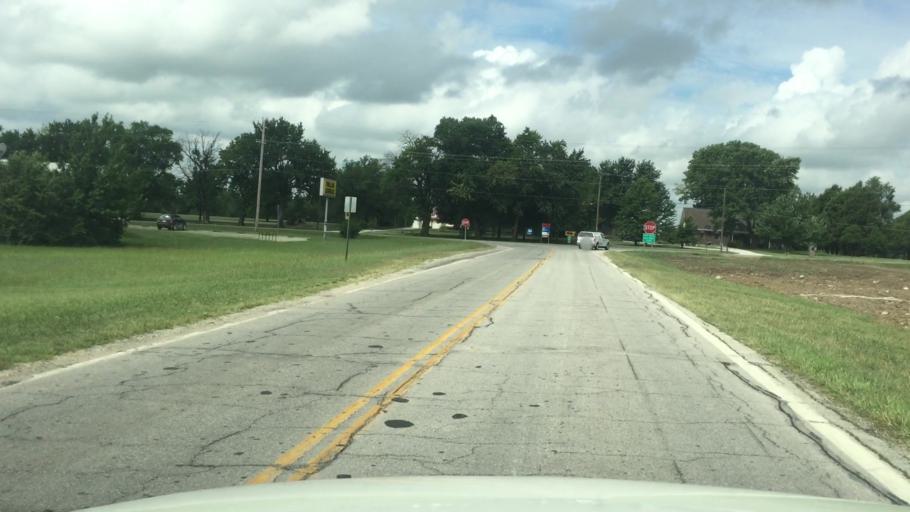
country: US
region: Kansas
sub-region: Allen County
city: Humboldt
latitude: 37.8220
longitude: -95.4355
